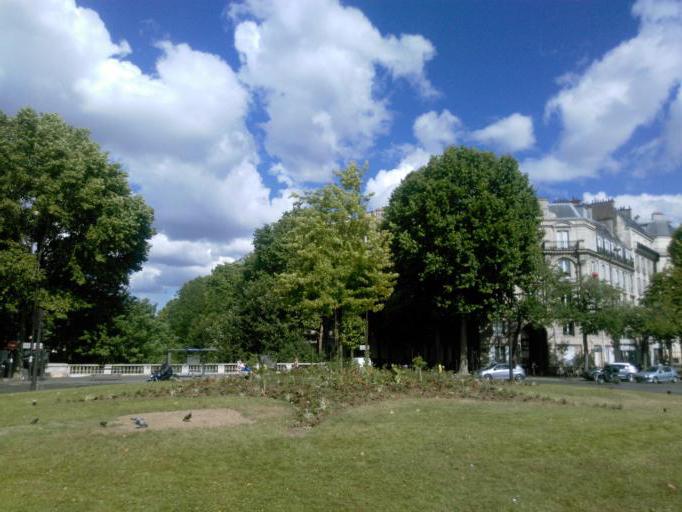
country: FR
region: Ile-de-France
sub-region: Departement des Hauts-de-Seine
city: Clichy
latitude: 48.8874
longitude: 2.3047
